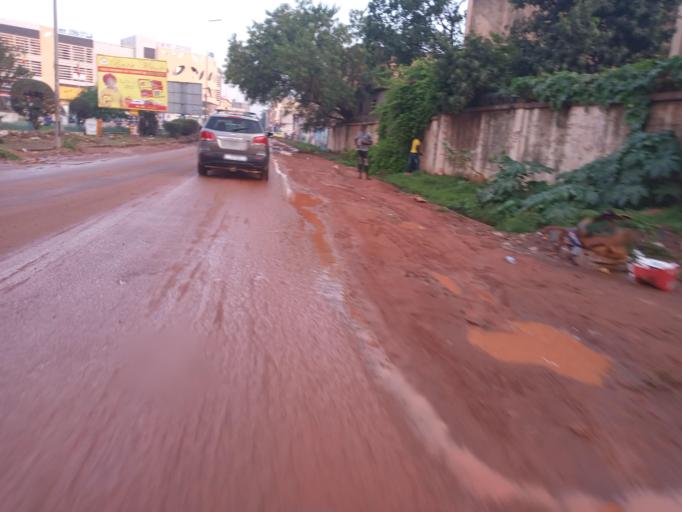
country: ML
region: Bamako
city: Bamako
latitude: 12.6269
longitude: -8.0355
